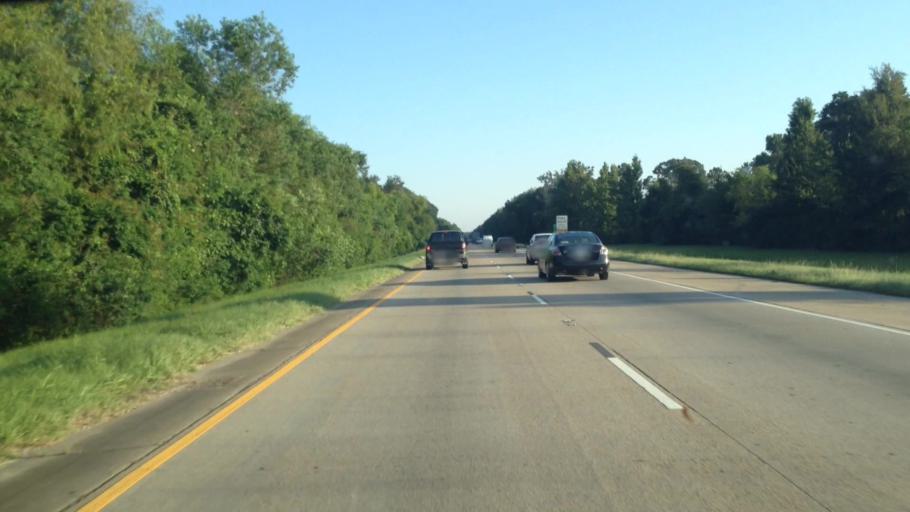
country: US
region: Louisiana
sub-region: Ascension Parish
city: Prairieville
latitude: 30.2840
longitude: -90.9893
